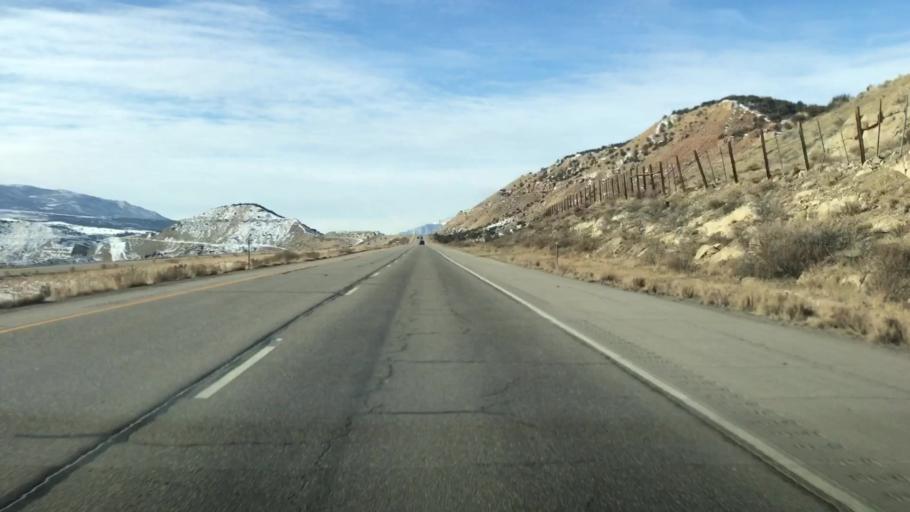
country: US
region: Colorado
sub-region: Garfield County
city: Rifle
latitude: 39.5115
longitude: -107.8704
